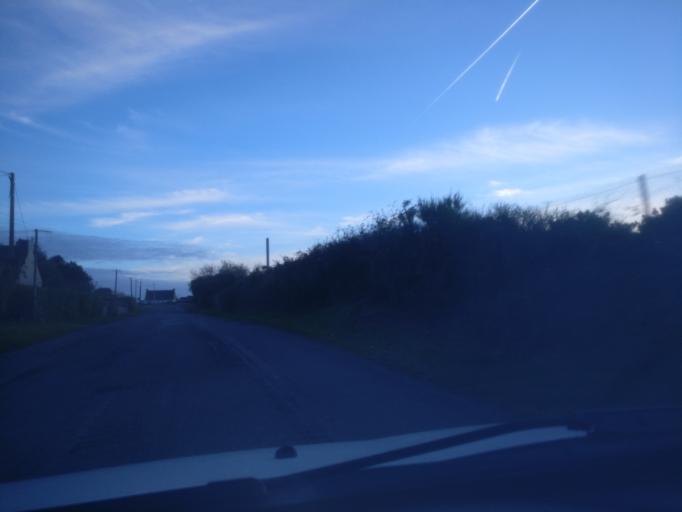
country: FR
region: Brittany
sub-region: Departement des Cotes-d'Armor
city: Tregastel
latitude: 48.8142
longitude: -3.4752
